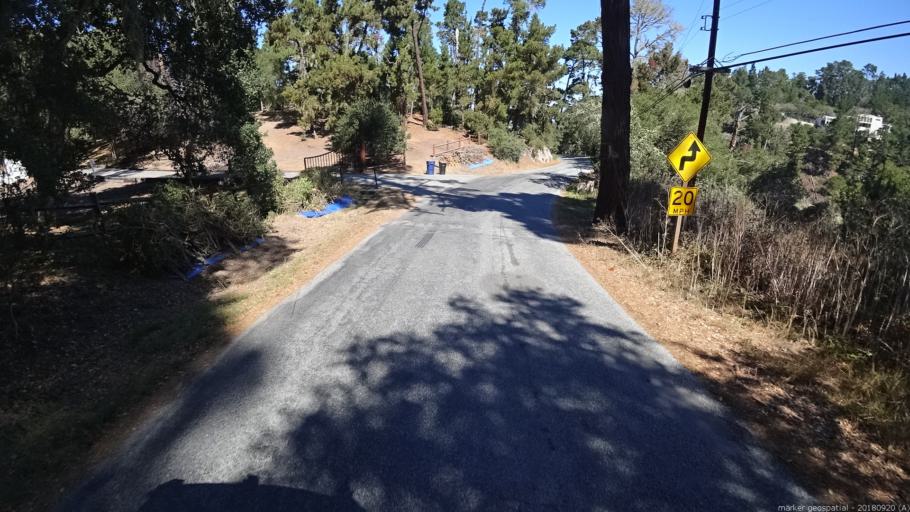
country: US
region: California
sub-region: Monterey County
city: Monterey
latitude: 36.5731
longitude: -121.8916
